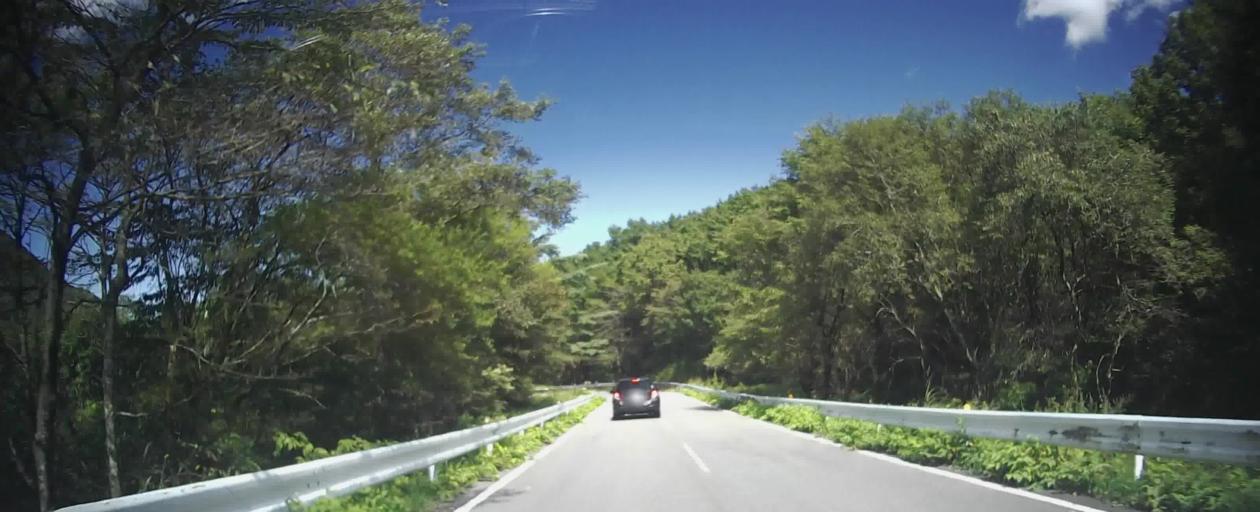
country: JP
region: Gunma
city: Shibukawa
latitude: 36.4691
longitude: 138.8847
